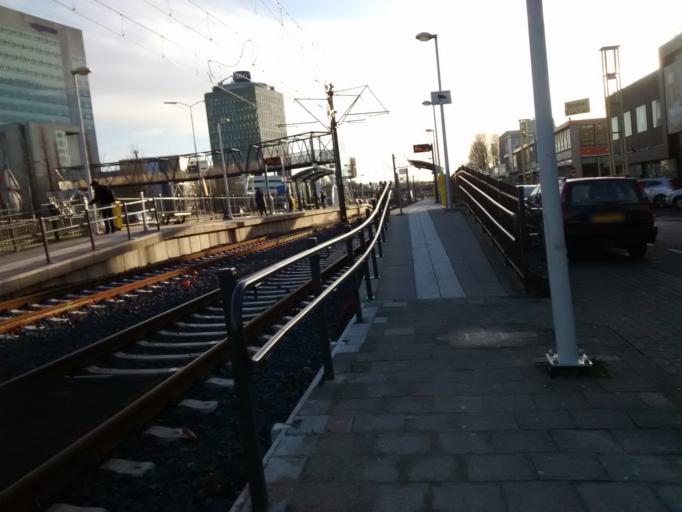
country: NL
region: Utrecht
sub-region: Gemeente Utrecht
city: Lunetten
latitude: 52.0636
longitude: 5.1075
